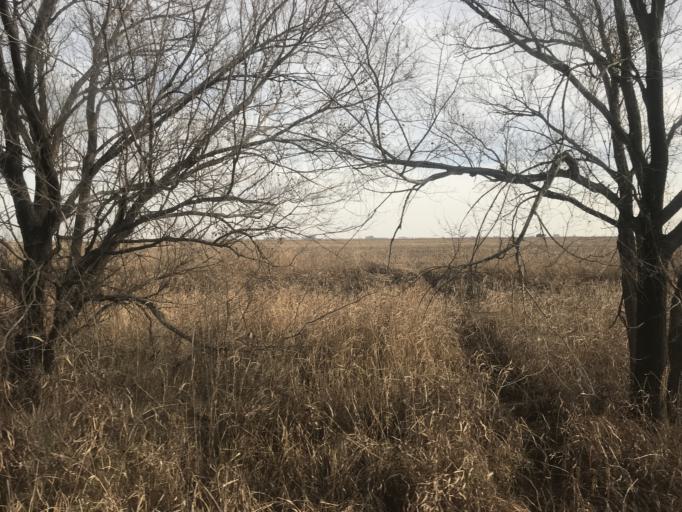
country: AR
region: Cordoba
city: Pilar
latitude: -31.7017
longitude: -63.8686
